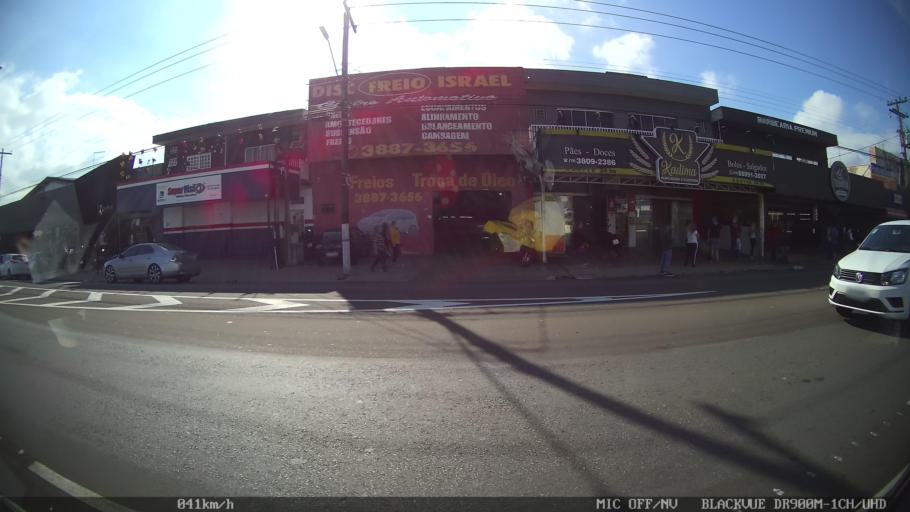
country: BR
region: Sao Paulo
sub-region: Hortolandia
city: Hortolandia
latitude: -22.8807
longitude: -47.1966
